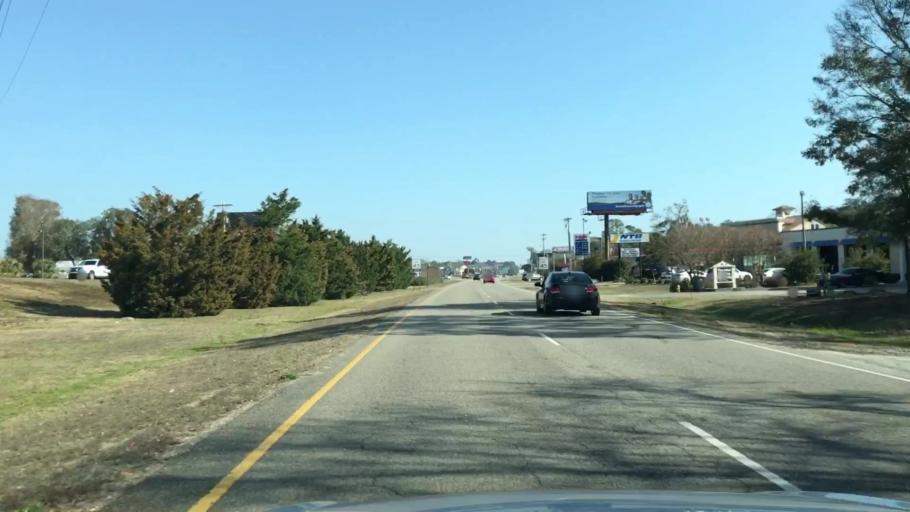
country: US
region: South Carolina
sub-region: Horry County
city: Garden City
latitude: 33.5747
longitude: -79.0276
